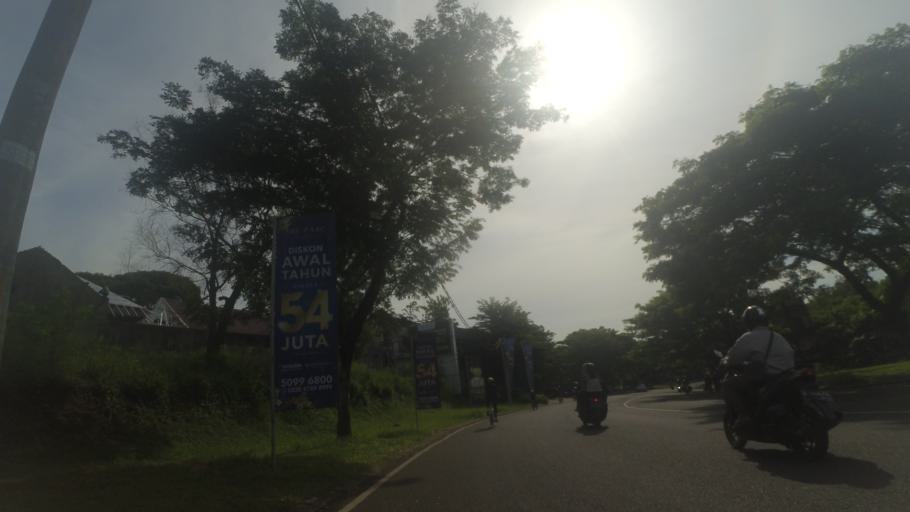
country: ID
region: West Java
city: Pamulang
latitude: -6.3423
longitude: 106.7695
